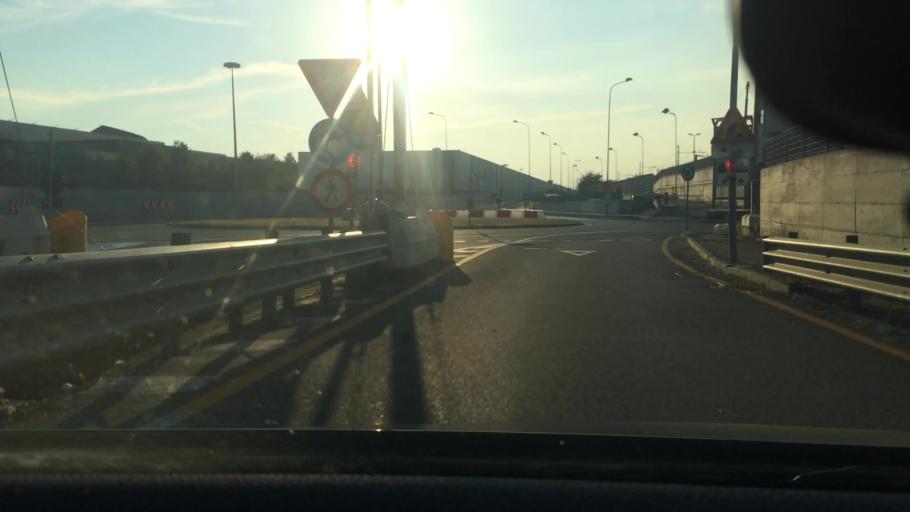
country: IT
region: Lombardy
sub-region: Citta metropolitana di Milano
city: Pero
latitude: 45.5214
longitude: 9.0866
